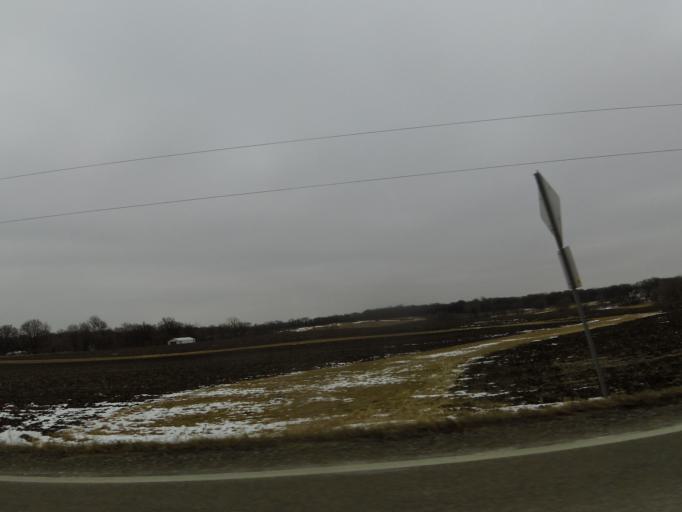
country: US
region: Minnesota
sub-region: Carver County
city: Watertown
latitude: 45.0105
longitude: -93.8487
